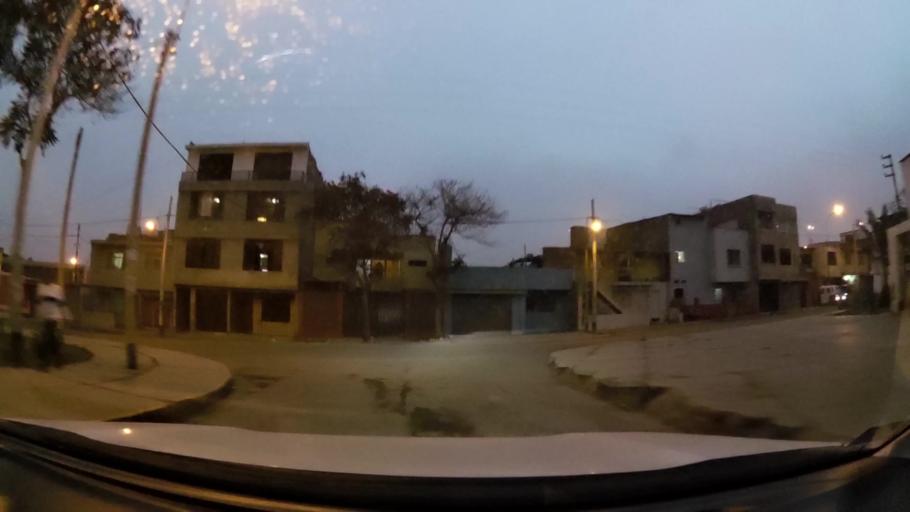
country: PE
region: Lima
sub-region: Lima
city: Surco
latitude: -12.1448
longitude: -76.9761
